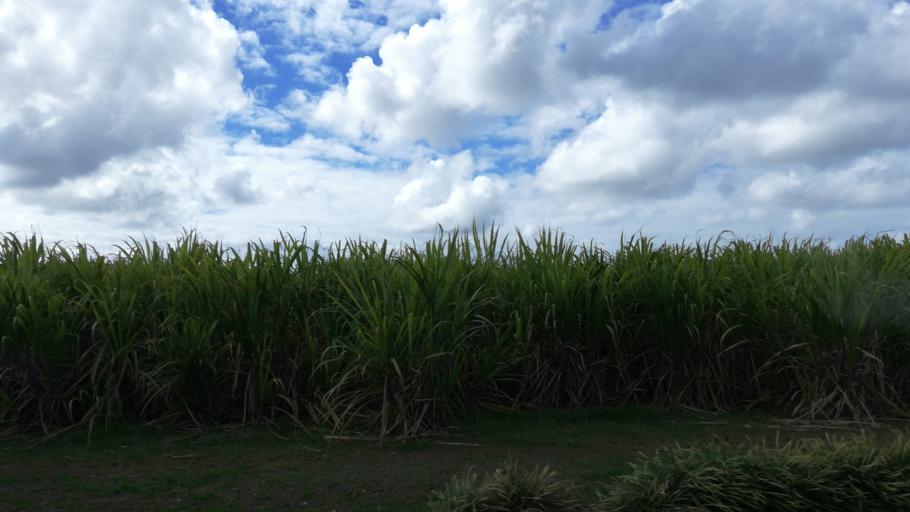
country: MU
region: Flacq
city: Camp de Masque
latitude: -20.2175
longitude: 57.6744
